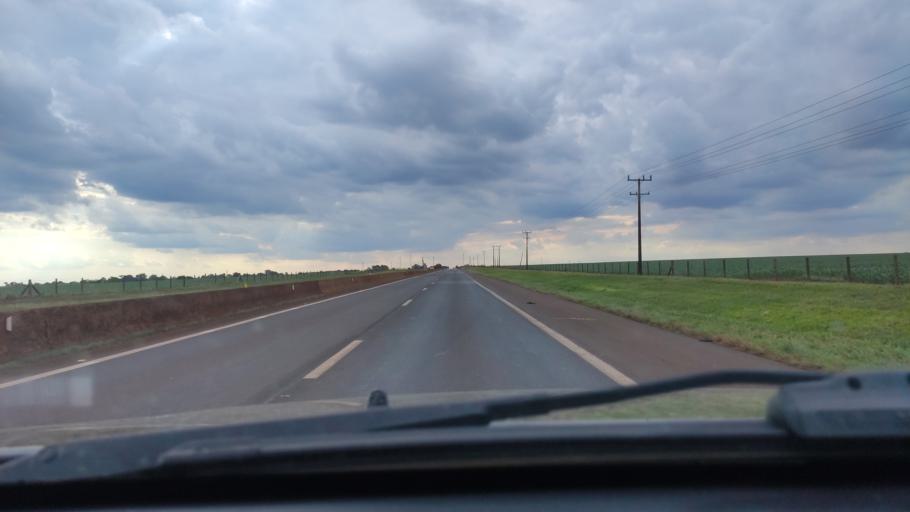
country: BR
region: Sao Paulo
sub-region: Palmital
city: Palmital
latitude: -22.8202
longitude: -50.0450
